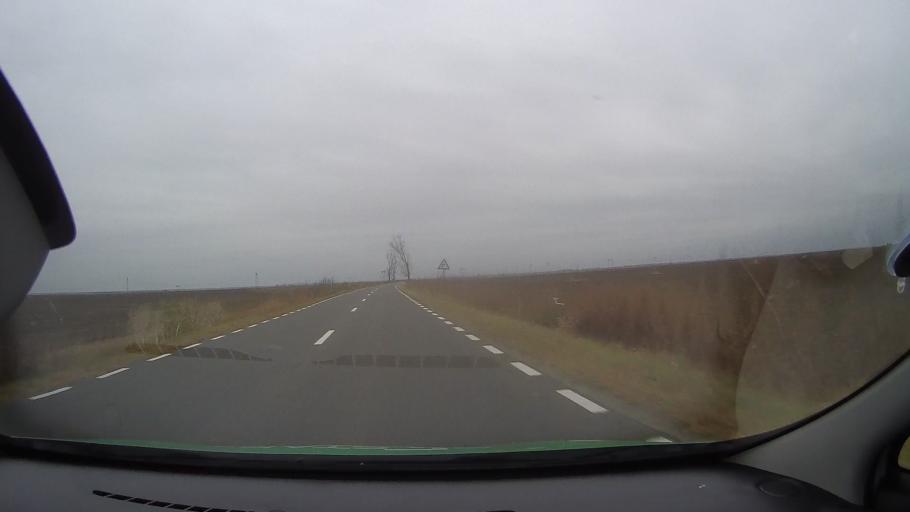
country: RO
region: Ialomita
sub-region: Comuna Gheorghe Lazar
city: Gheorghe Lazar
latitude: 44.6592
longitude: 27.4123
